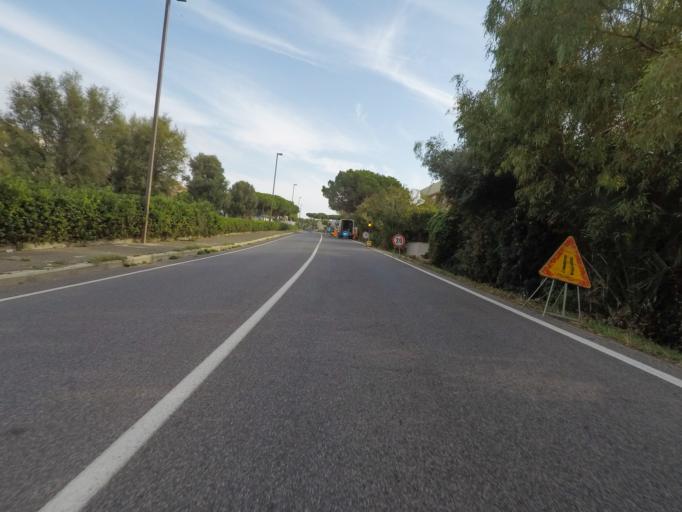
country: IT
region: Latium
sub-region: Citta metropolitana di Roma Capitale
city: Santa Marinella
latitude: 42.0352
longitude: 11.8337
